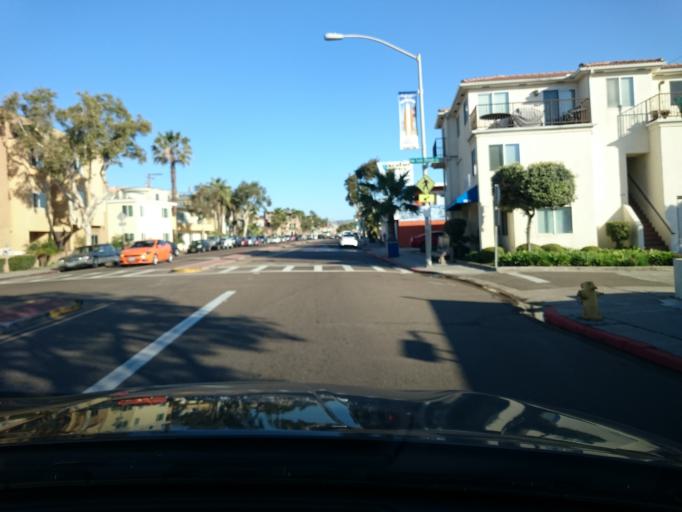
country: US
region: California
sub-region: San Diego County
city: La Jolla
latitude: 32.7761
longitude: -117.2523
